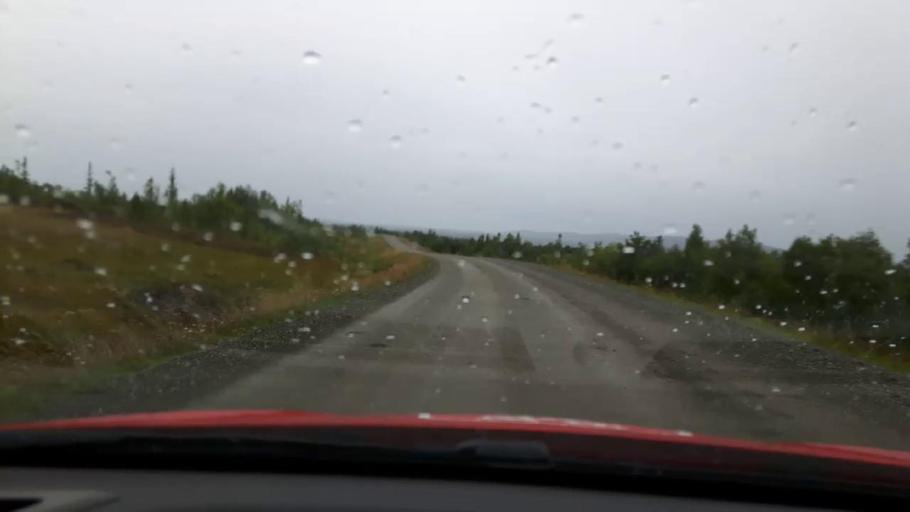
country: NO
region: Nord-Trondelag
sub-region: Meraker
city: Meraker
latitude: 63.6113
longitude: 12.2765
